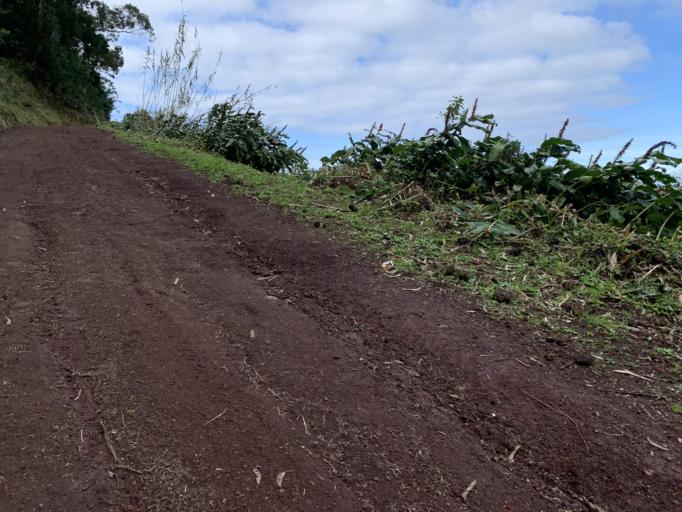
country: PT
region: Azores
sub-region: Ribeira Grande
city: Rabo de Peixe
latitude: 37.8039
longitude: -25.5023
